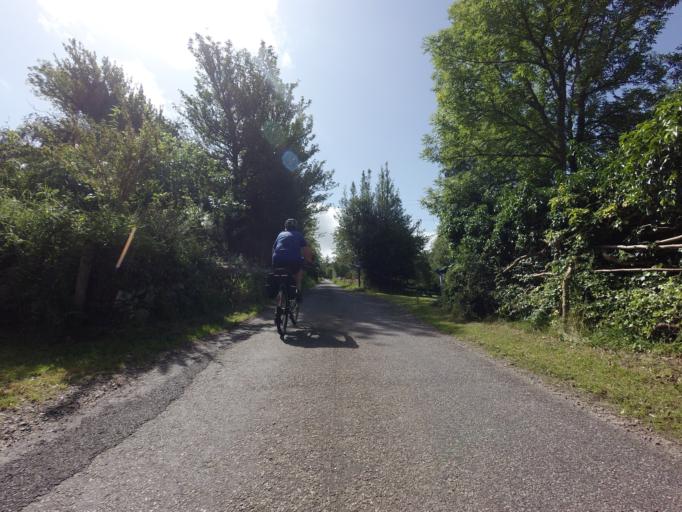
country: GB
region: Scotland
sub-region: Highland
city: Nairn
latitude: 57.5018
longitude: -3.9982
